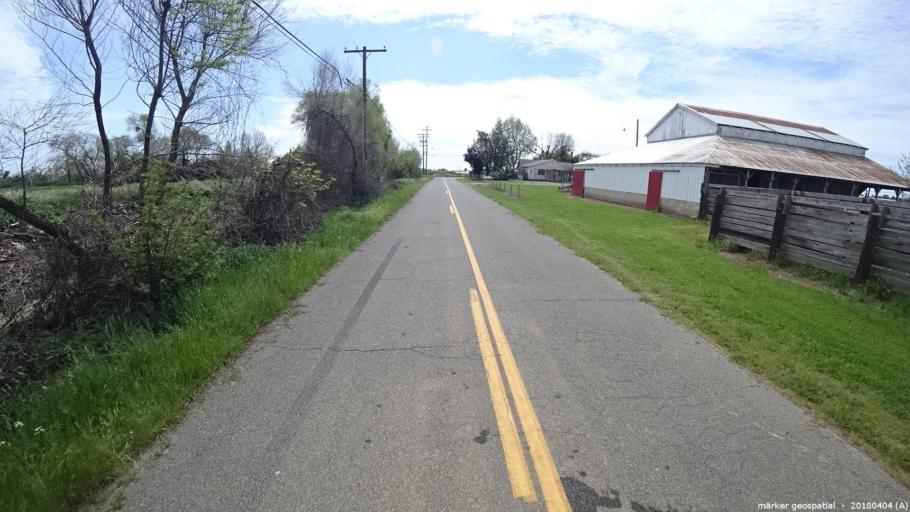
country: US
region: California
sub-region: Sacramento County
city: Herald
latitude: 38.2635
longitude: -121.2542
